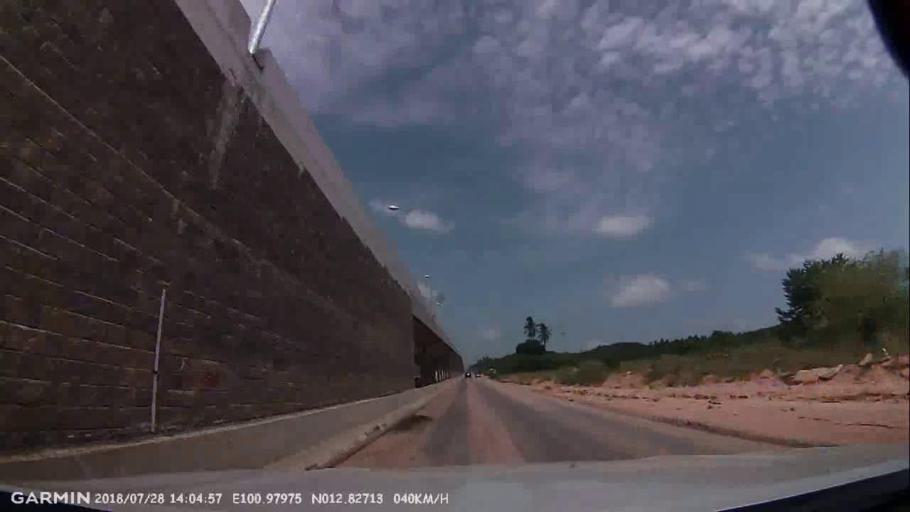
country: TH
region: Rayong
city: Ban Chang
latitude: 12.8271
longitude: 100.9799
